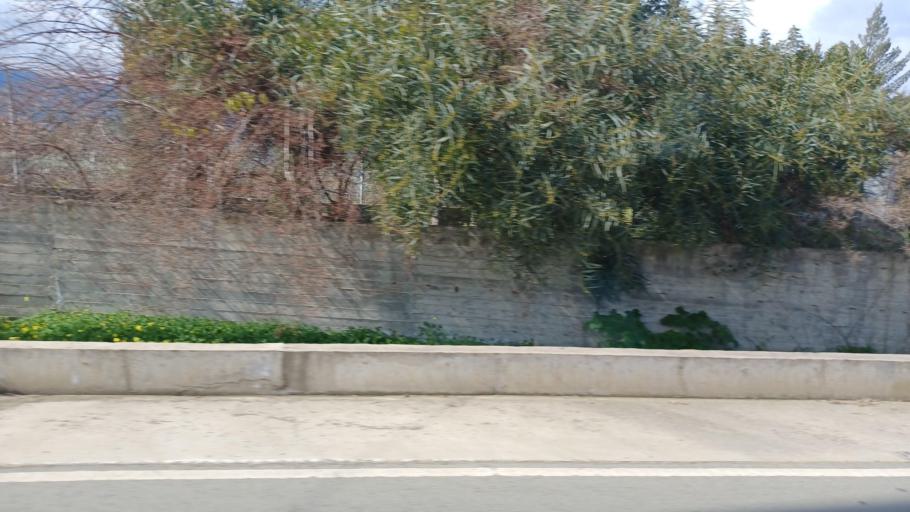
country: CY
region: Lefkosia
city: Lefka
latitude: 35.0799
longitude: 32.8943
